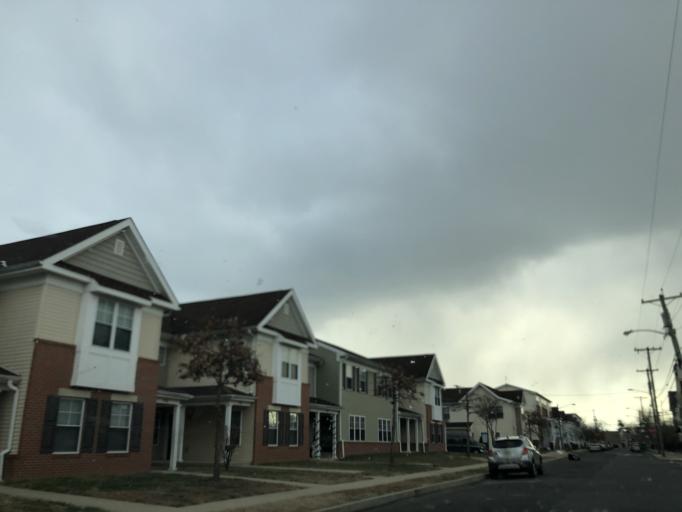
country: US
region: New Jersey
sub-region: Camden County
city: Camden
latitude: 39.9228
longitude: -75.1141
